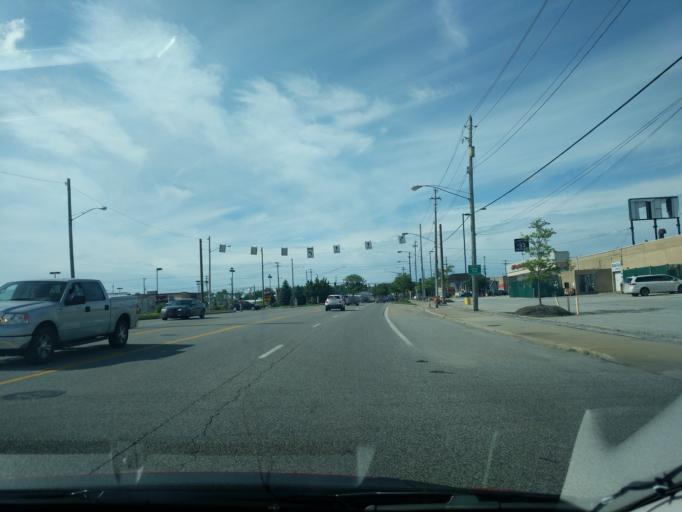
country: US
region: Ohio
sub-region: Cuyahoga County
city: North Randall
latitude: 41.4335
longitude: -81.5262
